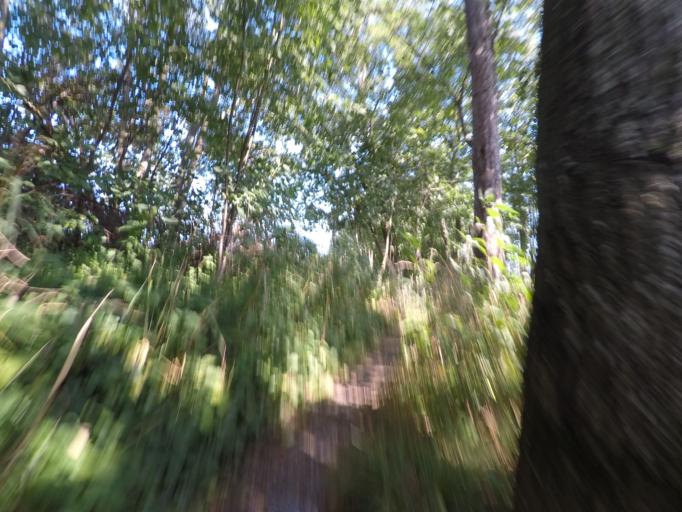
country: DE
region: Baden-Wuerttemberg
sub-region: Regierungsbezirk Stuttgart
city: Hildrizhausen
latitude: 48.6516
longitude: 8.9723
